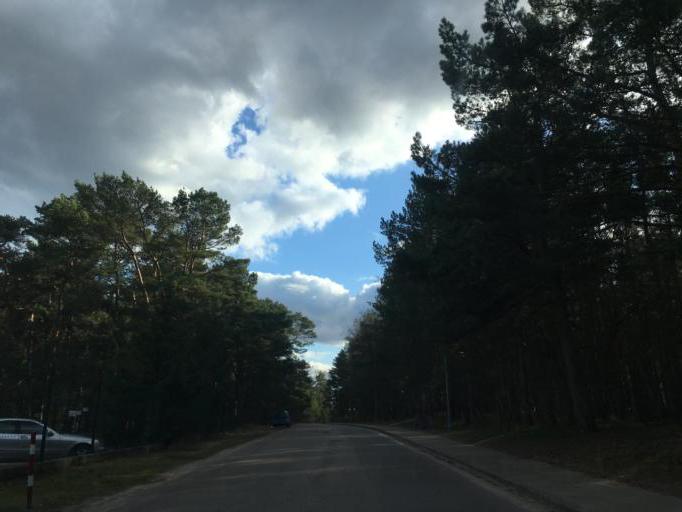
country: PL
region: Pomeranian Voivodeship
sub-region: Powiat gdanski
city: Cedry Wielkie
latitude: 54.3472
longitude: 18.8349
